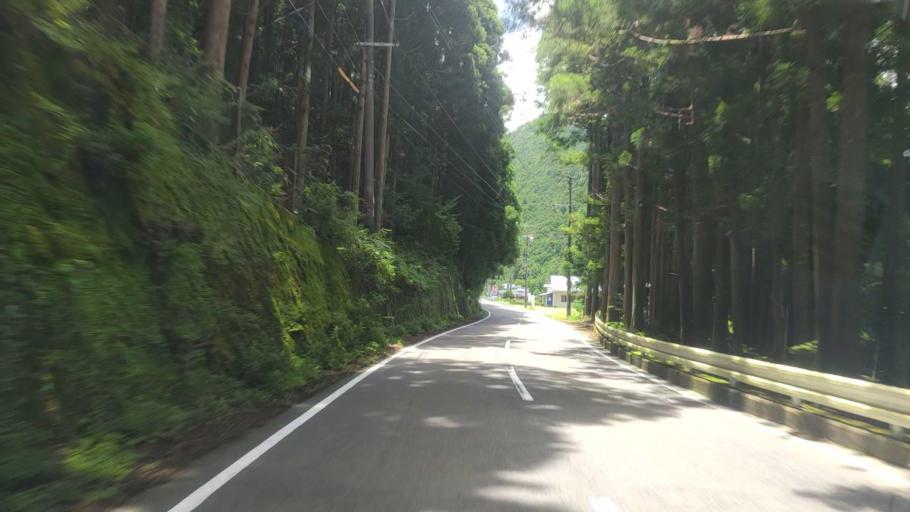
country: JP
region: Mie
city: Owase
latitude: 33.9669
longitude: 136.0612
